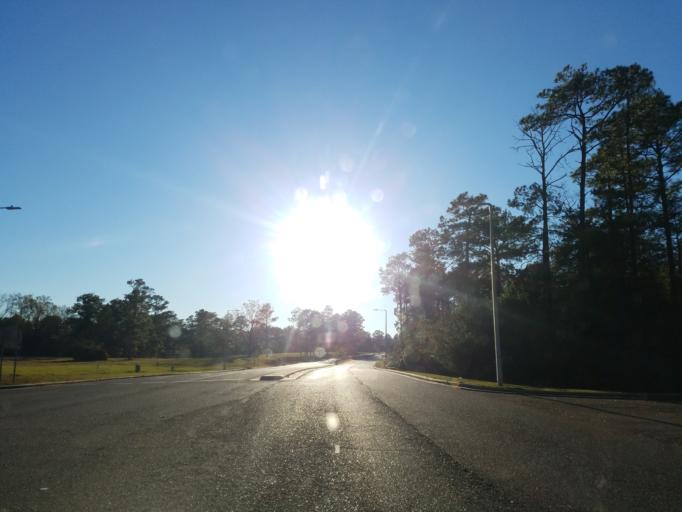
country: US
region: Mississippi
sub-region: Lamar County
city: Arnold Line
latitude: 31.3551
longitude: -89.3610
